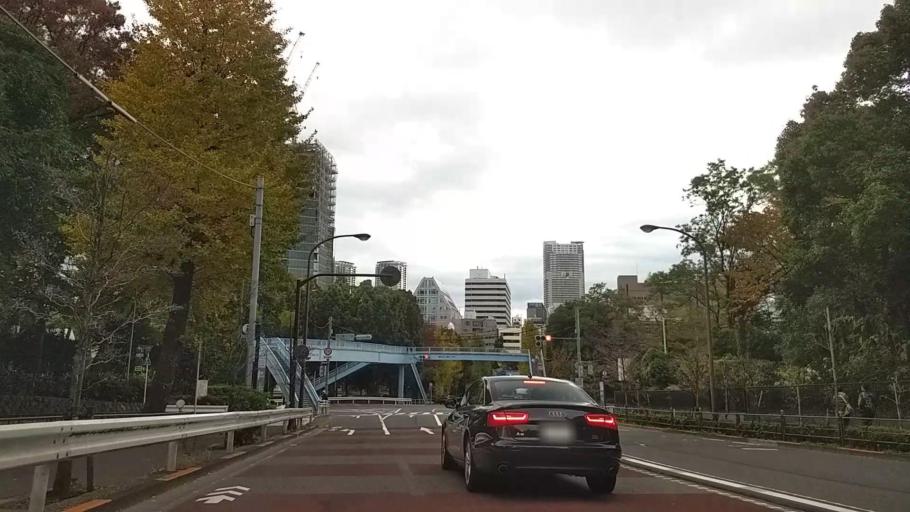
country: JP
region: Tokyo
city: Tokyo
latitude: 35.6599
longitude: 139.7481
